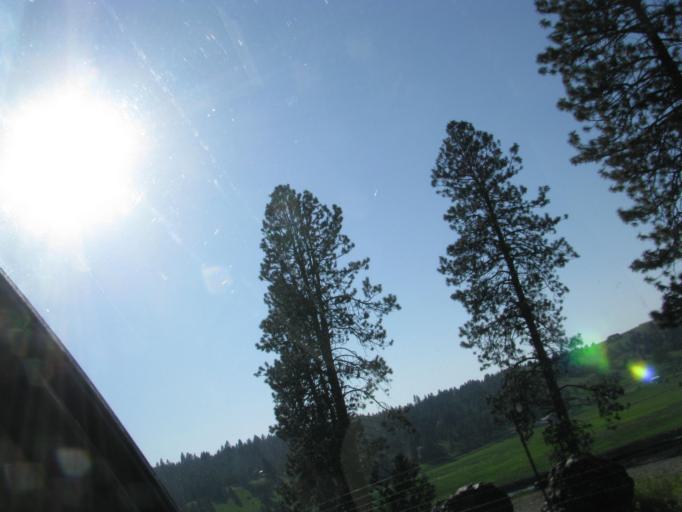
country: US
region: Washington
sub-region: Spokane County
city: Liberty Lake
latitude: 47.6082
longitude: -117.1229
